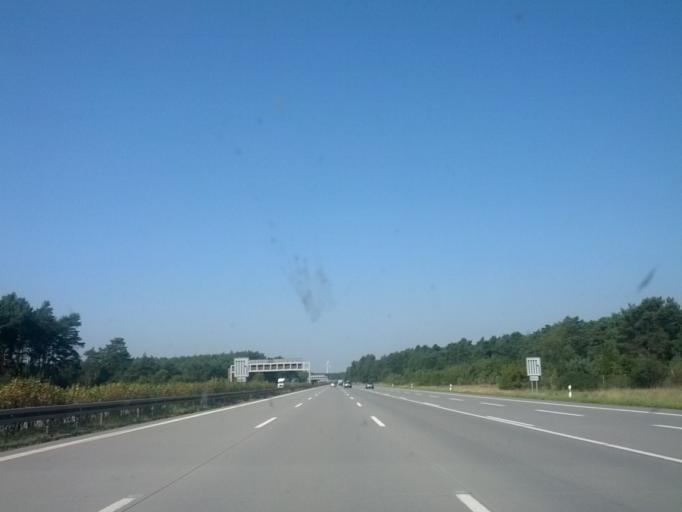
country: DE
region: Brandenburg
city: Erkner
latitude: 52.3241
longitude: 13.7337
